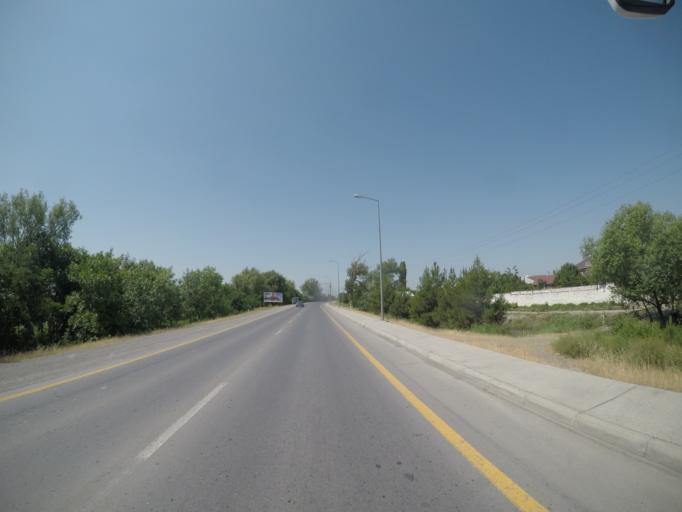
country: AZ
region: Agdas
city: Agdas
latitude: 40.6380
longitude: 47.4888
